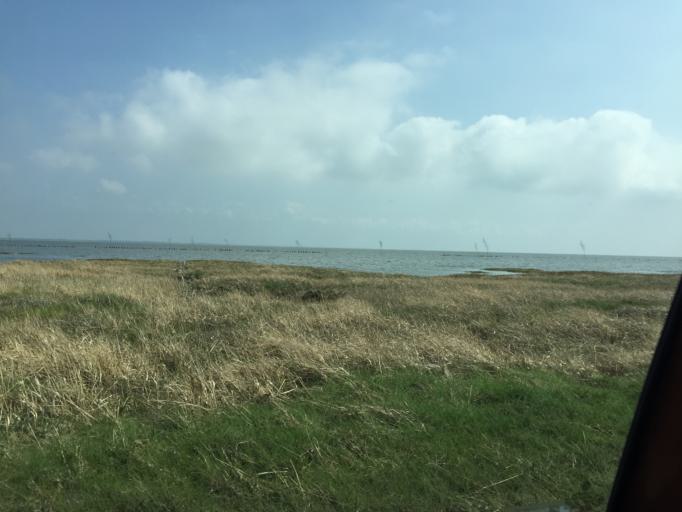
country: DK
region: South Denmark
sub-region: Esbjerg Kommune
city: Ribe
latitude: 55.2966
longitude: 8.6069
